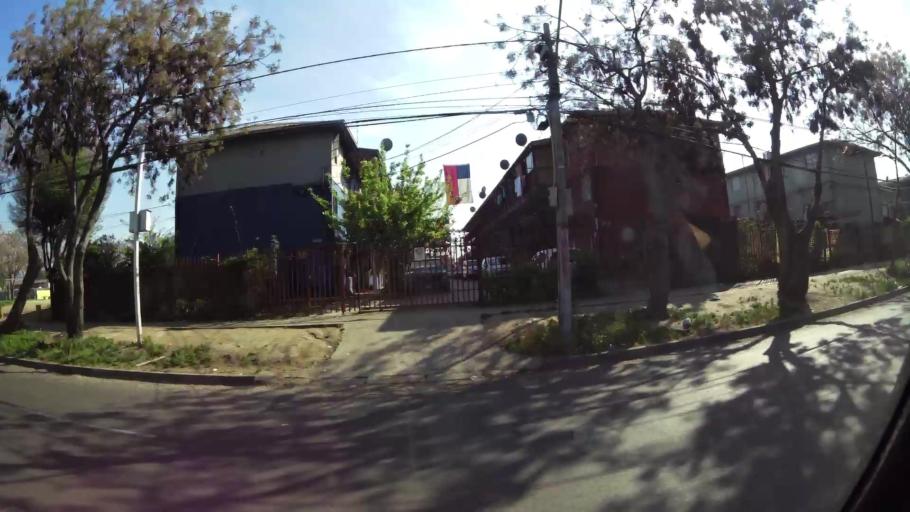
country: CL
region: Santiago Metropolitan
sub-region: Provincia de Santiago
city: Lo Prado
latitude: -33.4655
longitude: -70.7529
